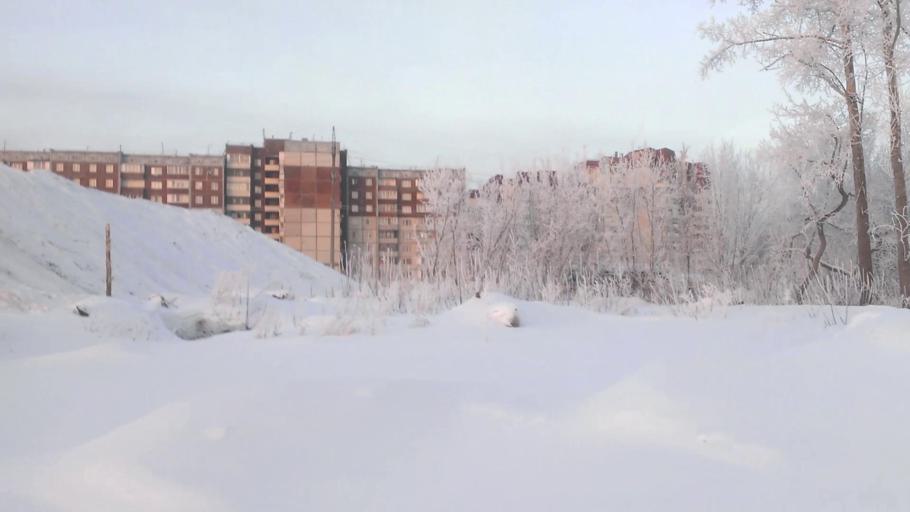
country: RU
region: Altai Krai
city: Novosilikatnyy
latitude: 53.3553
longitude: 83.6647
